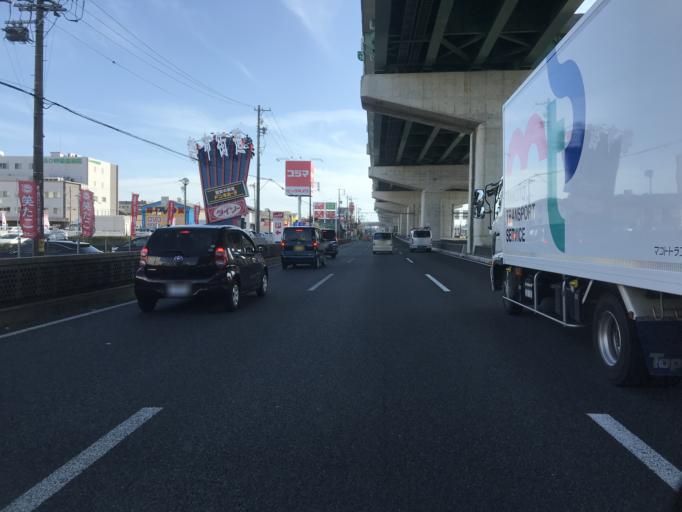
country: JP
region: Aichi
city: Iwakura
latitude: 35.2395
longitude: 136.8476
